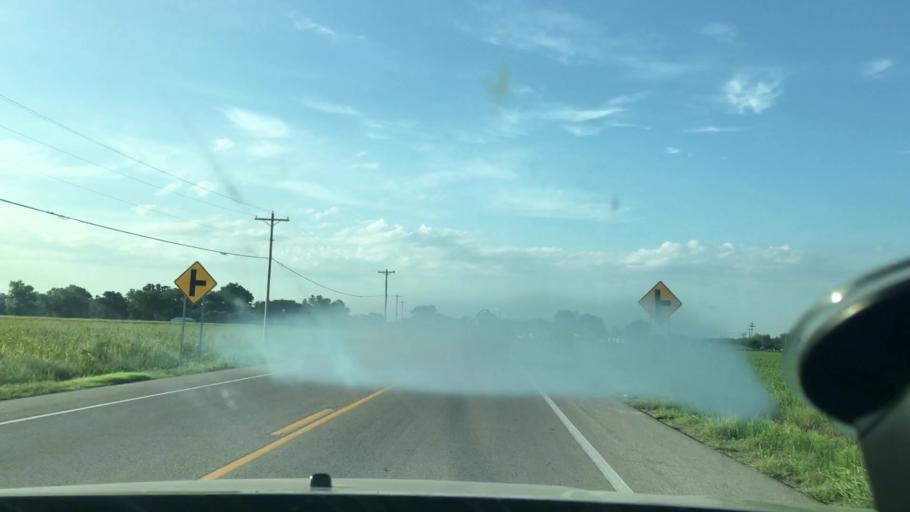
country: US
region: Oklahoma
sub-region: Garvin County
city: Wynnewood
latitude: 34.6555
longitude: -97.2017
